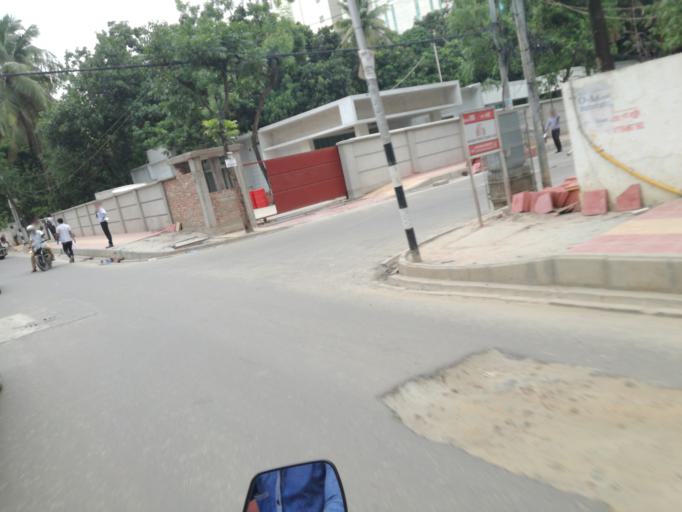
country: BD
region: Dhaka
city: Paltan
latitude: 23.7767
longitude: 90.4154
